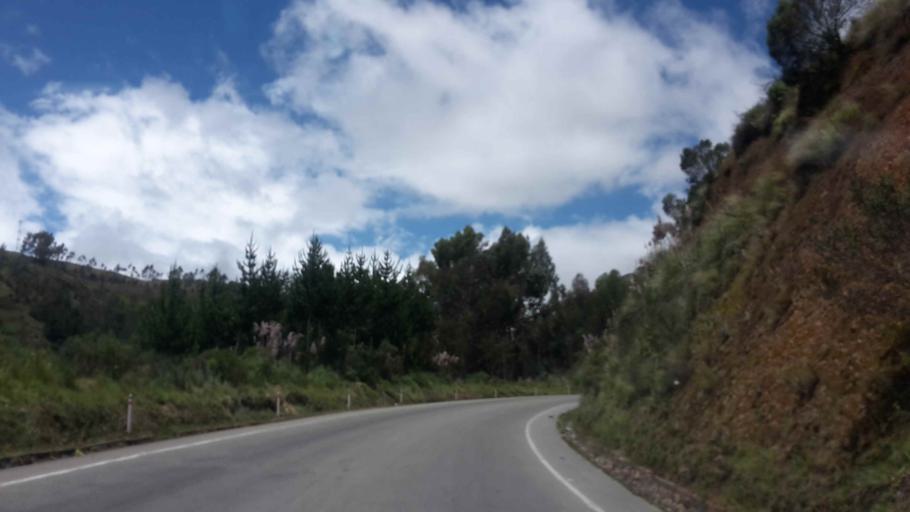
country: BO
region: Cochabamba
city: Colomi
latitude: -17.3160
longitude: -65.8720
